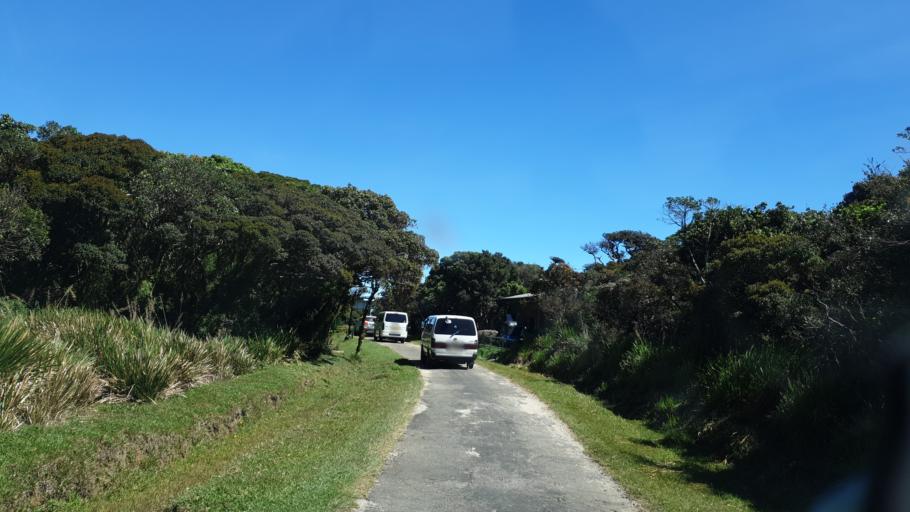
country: LK
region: Uva
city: Haputale
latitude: 6.8066
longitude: 80.8344
